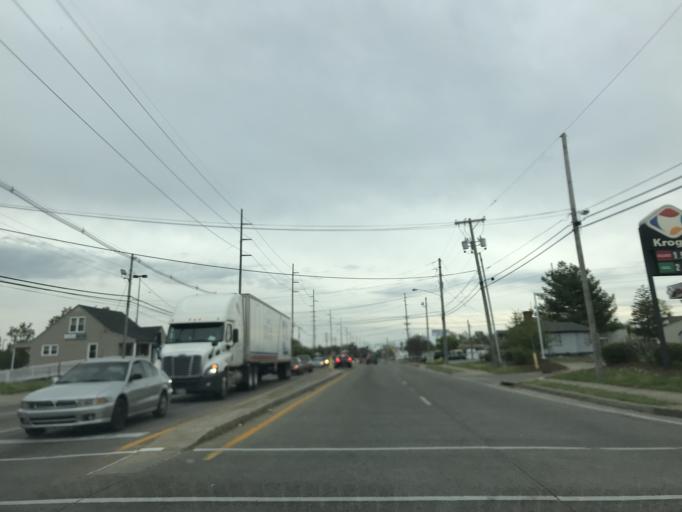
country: US
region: Kentucky
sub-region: Jefferson County
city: West Buechel
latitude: 38.1969
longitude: -85.6632
